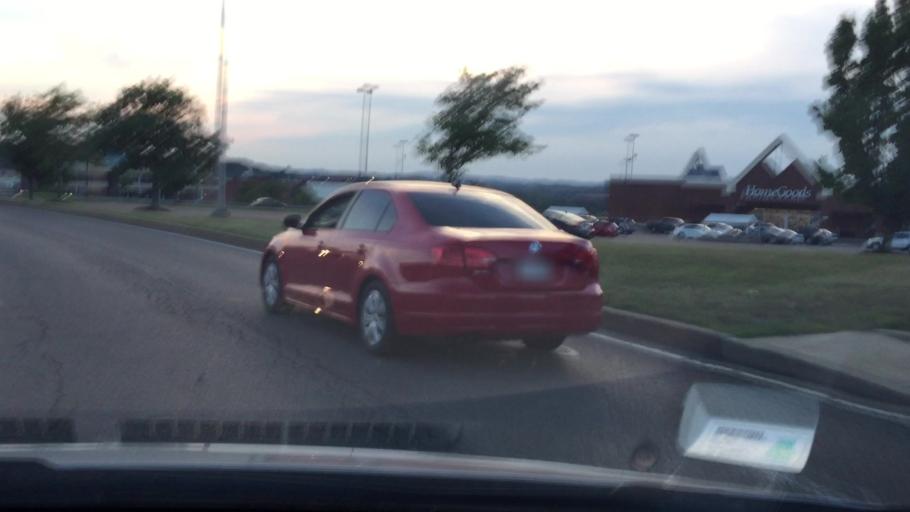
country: US
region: Pennsylvania
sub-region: Allegheny County
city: Oakdale
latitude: 40.4534
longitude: -80.1682
